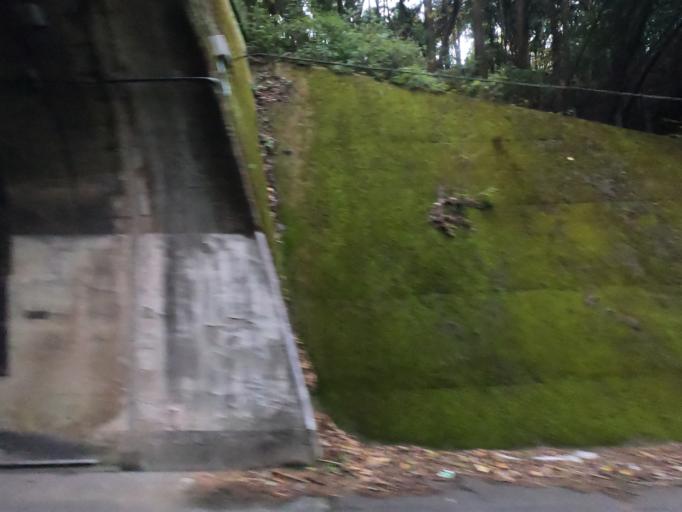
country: JP
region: Kumamoto
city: Minamata
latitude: 32.2467
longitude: 130.4927
